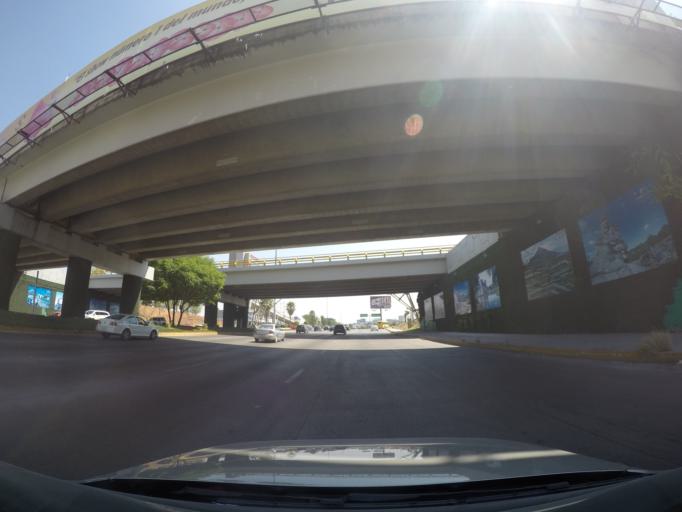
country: MX
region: Puebla
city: Tlazcalancingo
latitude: 19.0185
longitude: -98.2492
